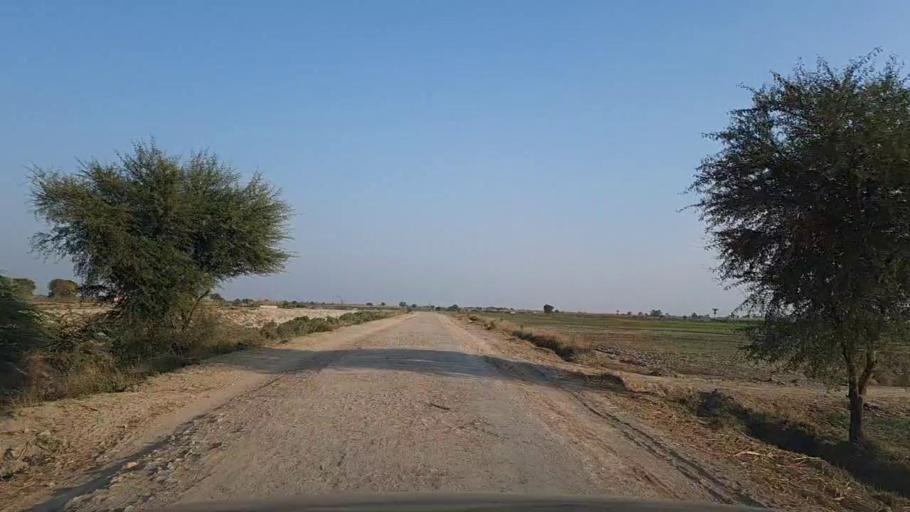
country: PK
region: Sindh
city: Tando Mittha Khan
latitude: 25.9409
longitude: 69.0741
